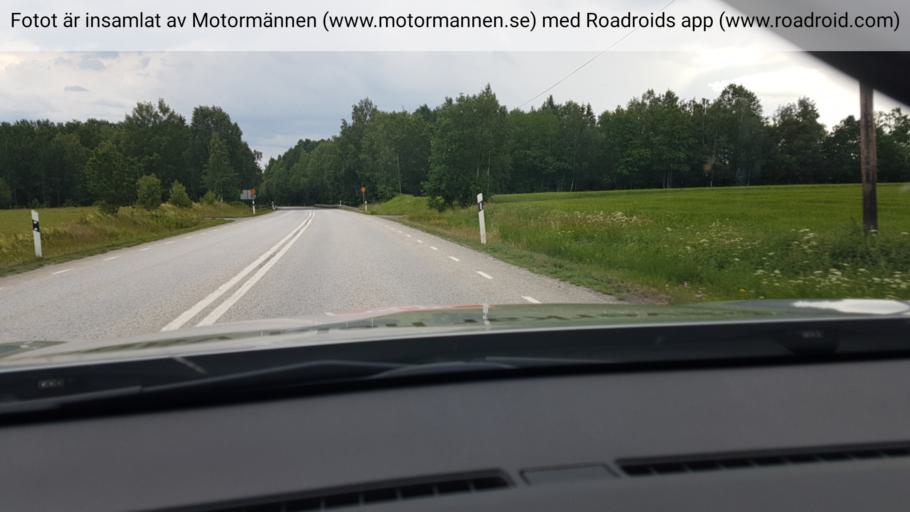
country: SE
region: Joenkoeping
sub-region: Habo Kommun
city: Habo
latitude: 57.9275
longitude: 14.0952
